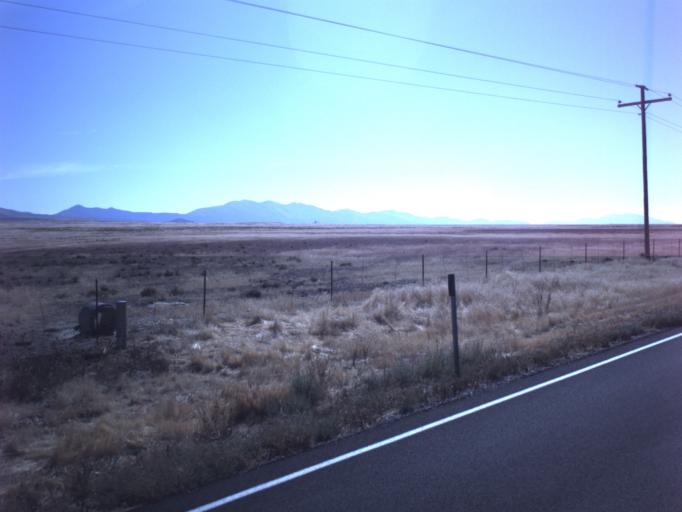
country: US
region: Utah
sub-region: Tooele County
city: Grantsville
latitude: 40.4286
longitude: -112.7488
